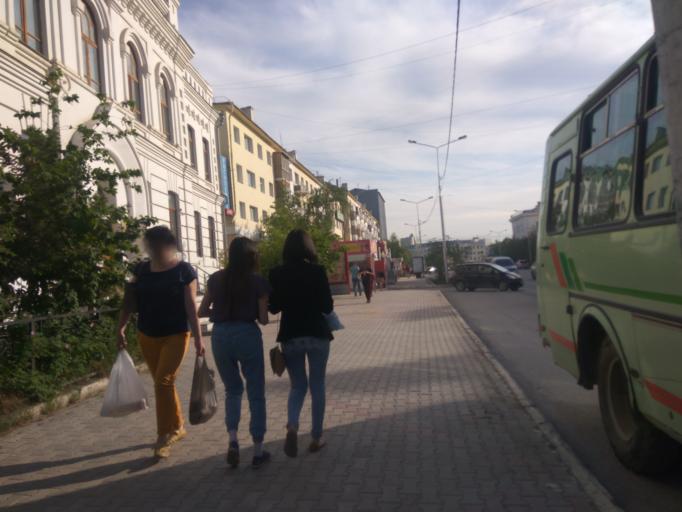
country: RU
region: Sakha
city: Yakutsk
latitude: 62.0247
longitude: 129.7248
